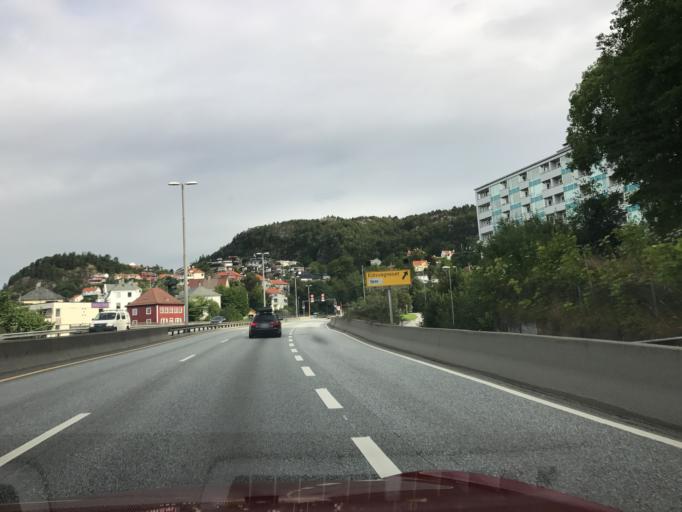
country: NO
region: Hordaland
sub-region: Bergen
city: Bergen
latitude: 60.4235
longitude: 5.3051
